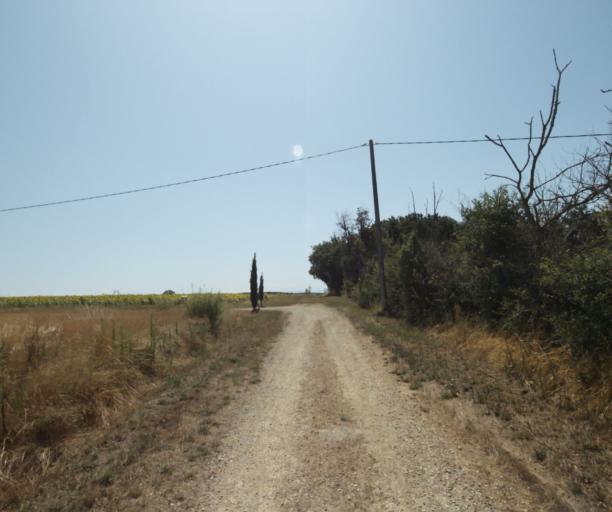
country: FR
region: Midi-Pyrenees
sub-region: Departement de la Haute-Garonne
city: Saint-Felix-Lauragais
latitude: 43.4519
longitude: 1.8506
